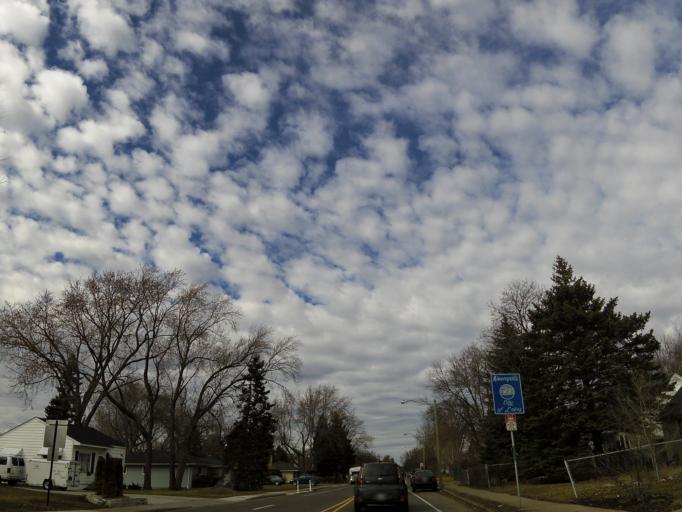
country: US
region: Minnesota
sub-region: Hennepin County
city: Edina
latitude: 44.8912
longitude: -93.3188
